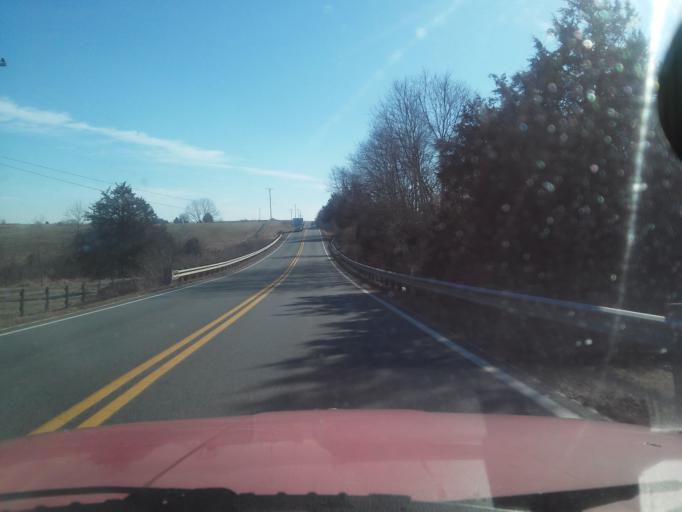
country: US
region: Virginia
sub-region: Orange County
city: Gordonsville
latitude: 38.0468
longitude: -78.1890
